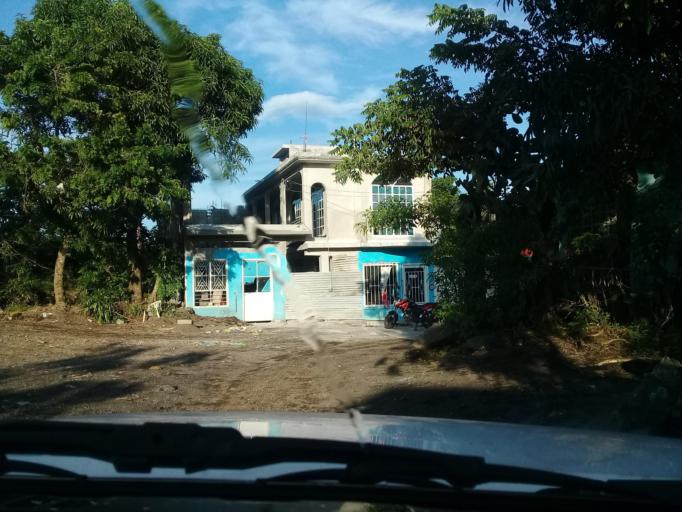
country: MX
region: Veracruz
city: Catemaco
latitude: 18.4232
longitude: -95.1004
